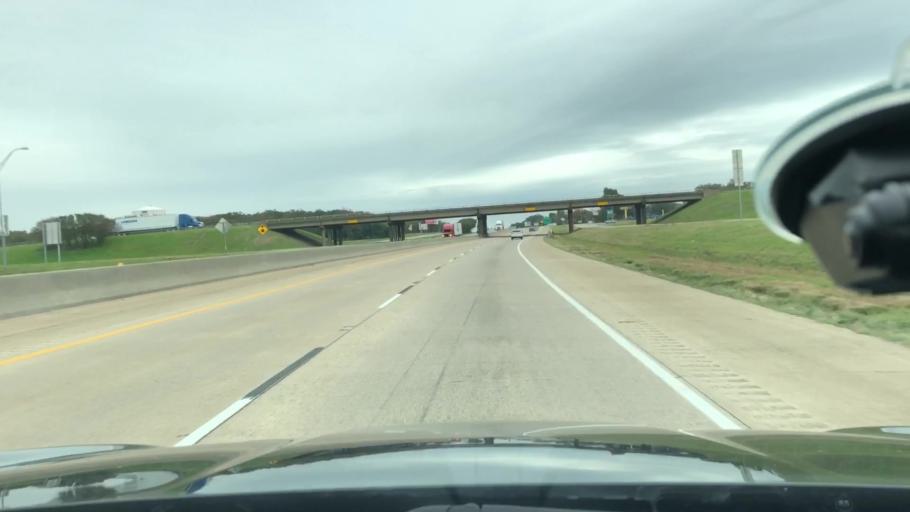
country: US
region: Texas
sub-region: Hopkins County
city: Sulphur Springs
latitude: 33.1204
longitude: -95.6359
